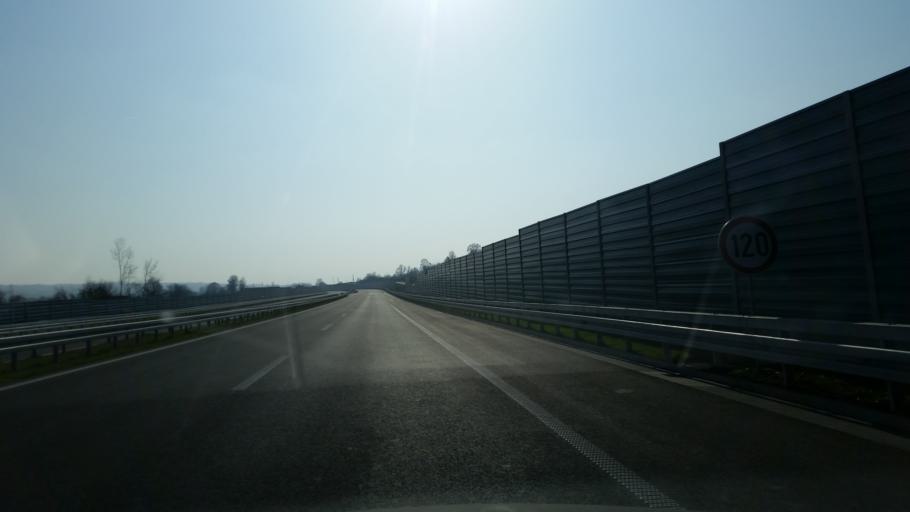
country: RS
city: Prislonica
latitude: 43.9658
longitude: 20.3959
